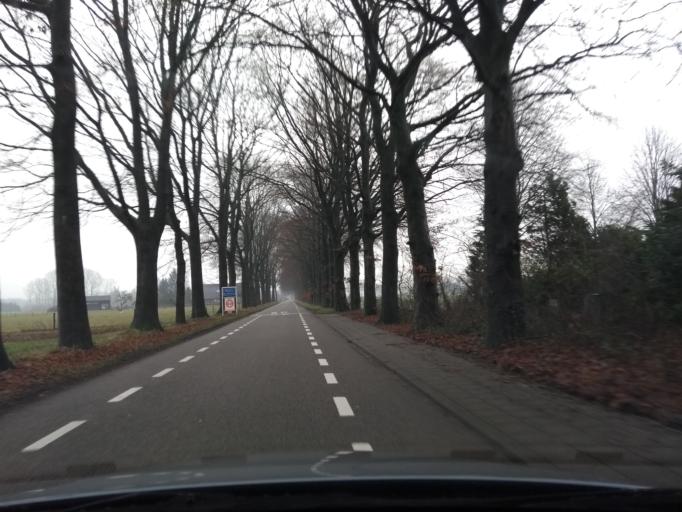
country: NL
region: Gelderland
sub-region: Gemeente Bronckhorst
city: Hengelo
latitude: 52.0481
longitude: 6.3188
